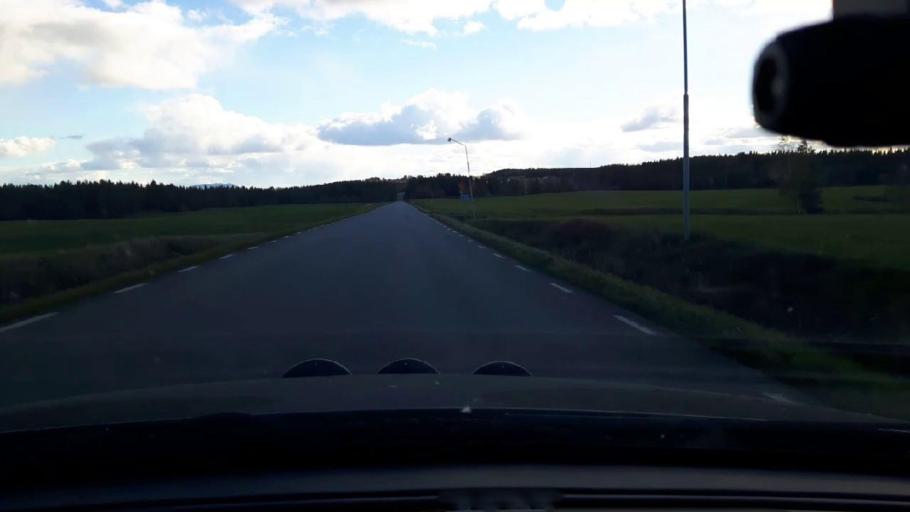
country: SE
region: Jaemtland
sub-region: Bergs Kommun
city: Hoverberg
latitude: 63.0350
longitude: 14.3454
